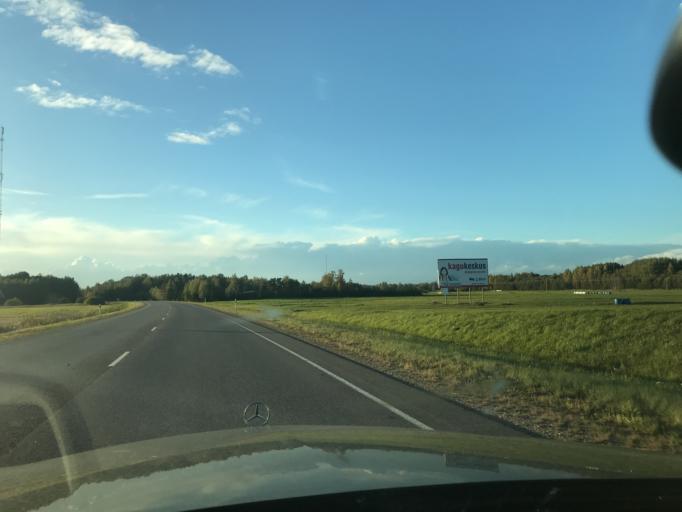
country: EE
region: Vorumaa
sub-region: Voru linn
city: Voru
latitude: 57.8573
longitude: 27.0176
